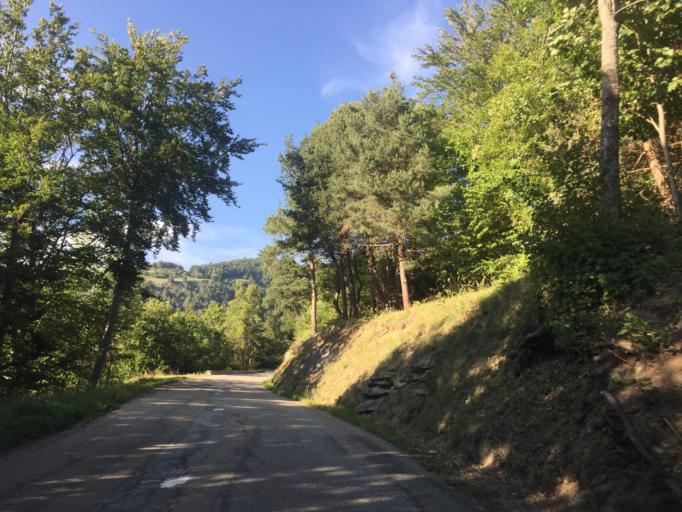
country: FR
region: Rhone-Alpes
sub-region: Departement de la Savoie
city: Moutiers
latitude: 45.5055
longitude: 6.5772
